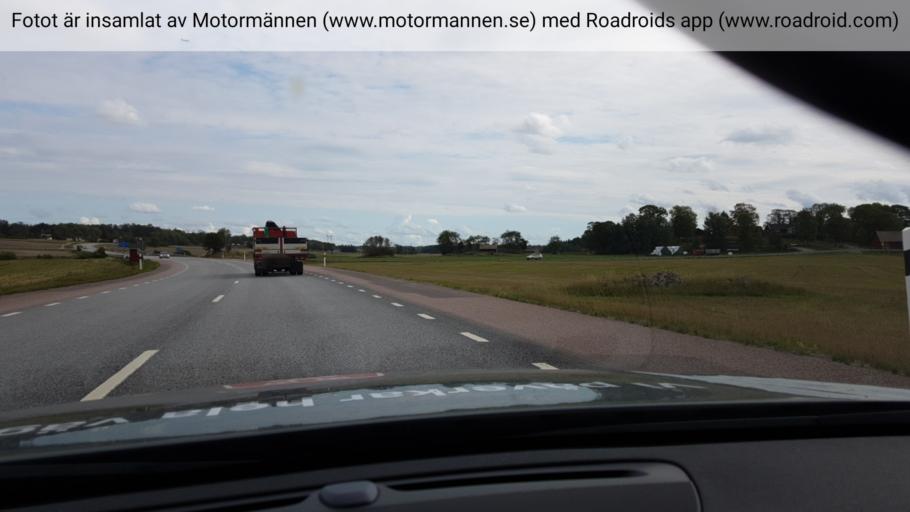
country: SE
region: Stockholm
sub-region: Sigtuna Kommun
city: Marsta
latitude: 59.7485
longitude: 17.9565
